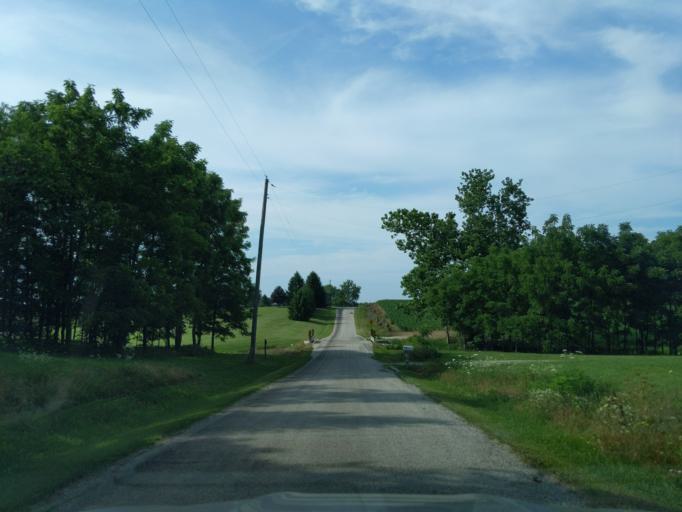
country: US
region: Indiana
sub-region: Ripley County
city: Osgood
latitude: 39.2097
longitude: -85.3893
